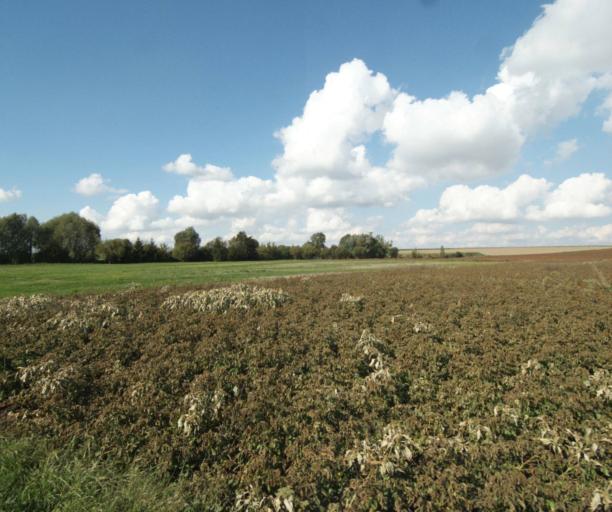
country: FR
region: Nord-Pas-de-Calais
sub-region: Departement du Nord
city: Herlies
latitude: 50.5735
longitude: 2.8417
